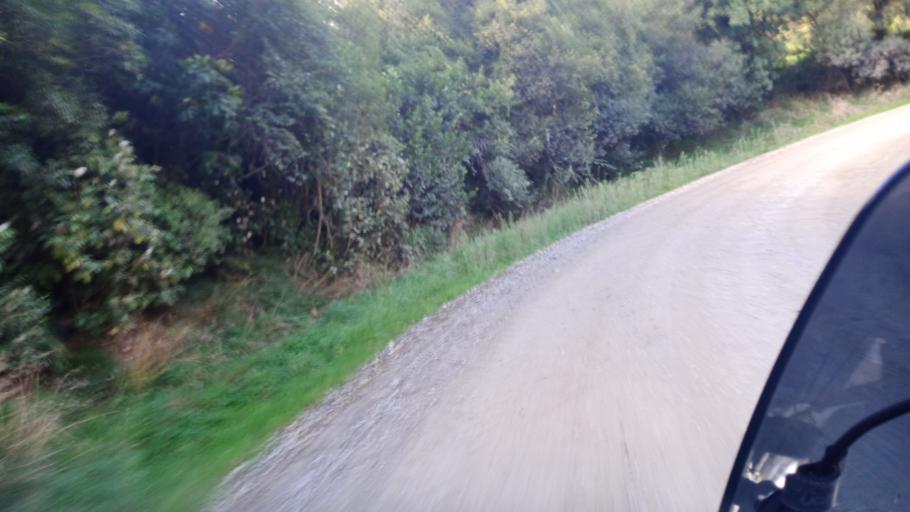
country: NZ
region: Gisborne
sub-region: Gisborne District
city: Gisborne
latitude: -38.5375
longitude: 177.5205
